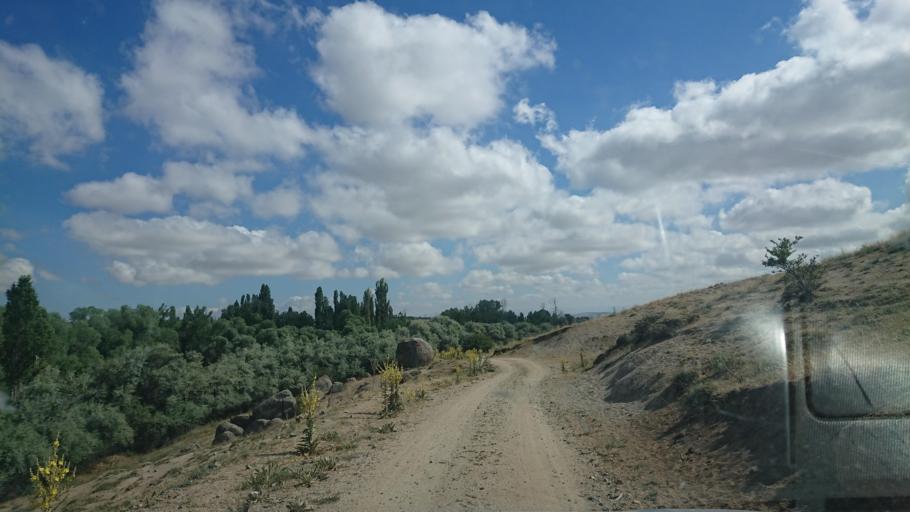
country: TR
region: Aksaray
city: Agacoren
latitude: 38.8538
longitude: 33.9360
